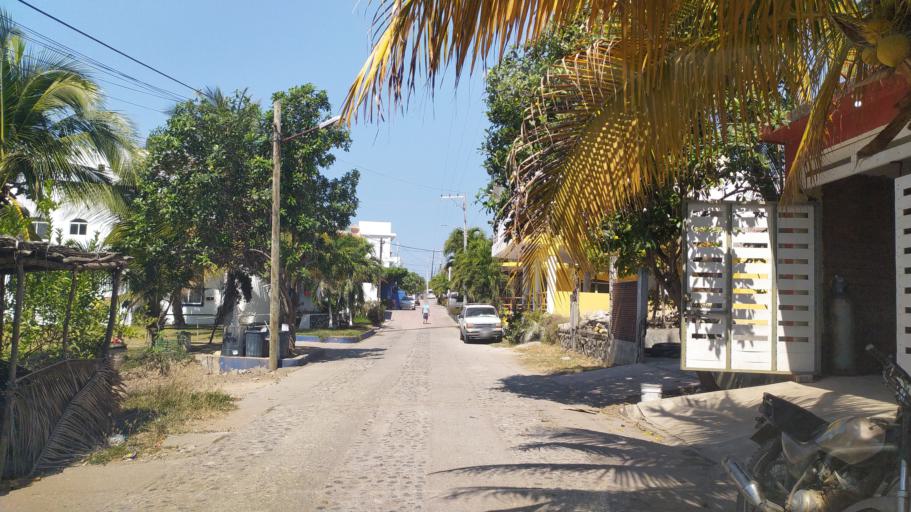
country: MX
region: Michoacan
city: Coahuayana Viejo
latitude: 18.5787
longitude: -103.6676
